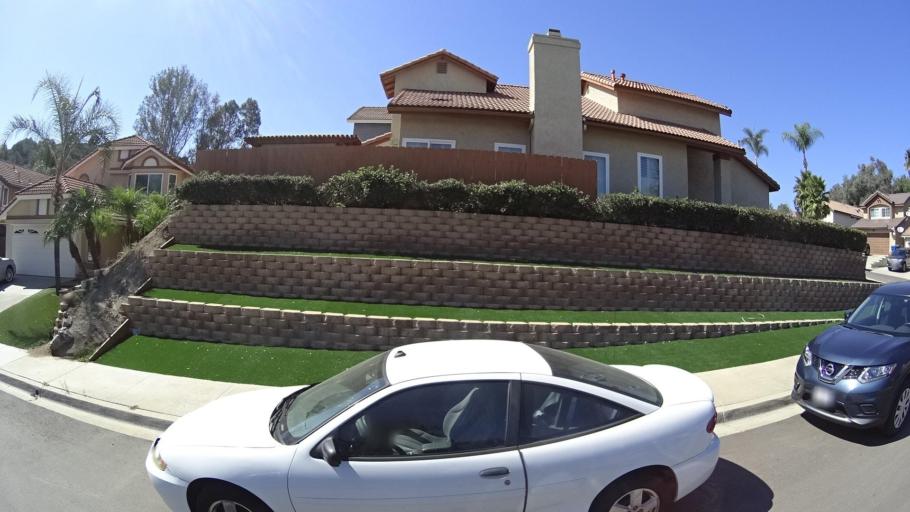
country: US
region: California
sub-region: San Diego County
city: Rancho San Diego
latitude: 32.7544
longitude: -116.9369
